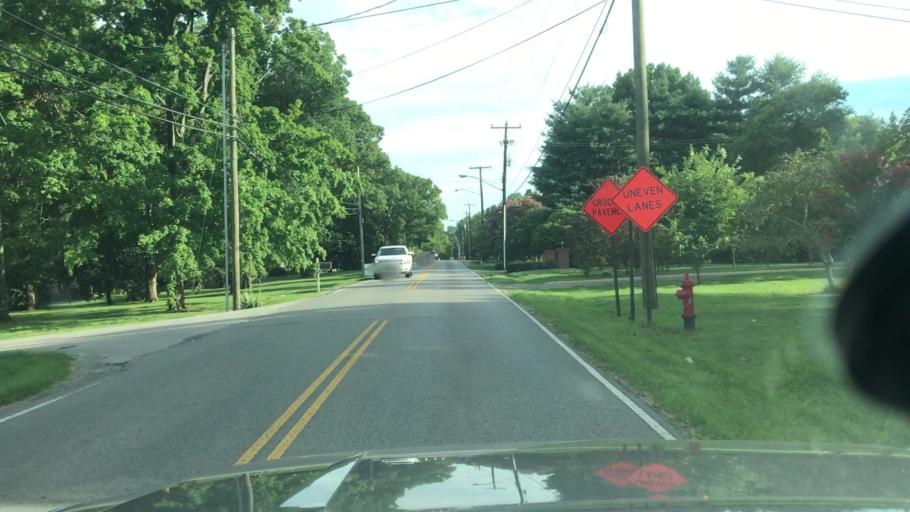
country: US
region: Tennessee
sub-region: Davidson County
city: Belle Meade
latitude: 36.1084
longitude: -86.8376
